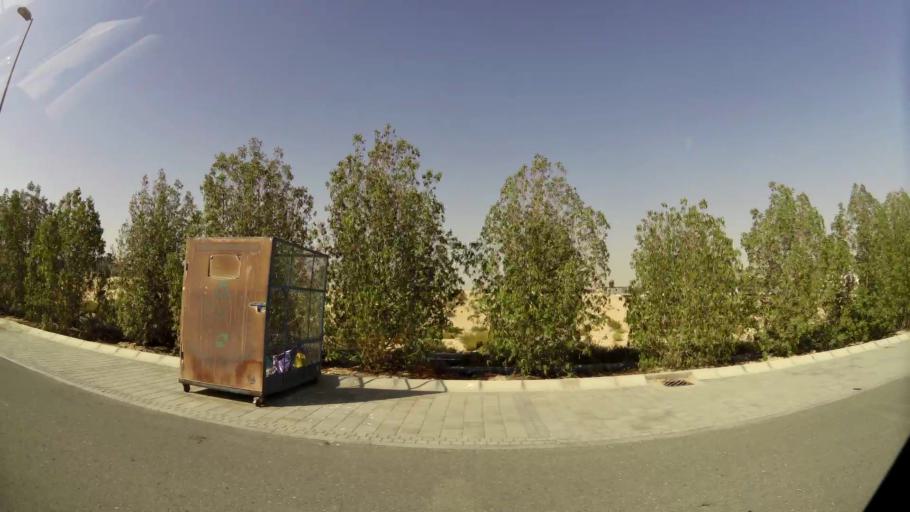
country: AE
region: Dubai
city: Dubai
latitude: 25.0711
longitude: 55.2151
